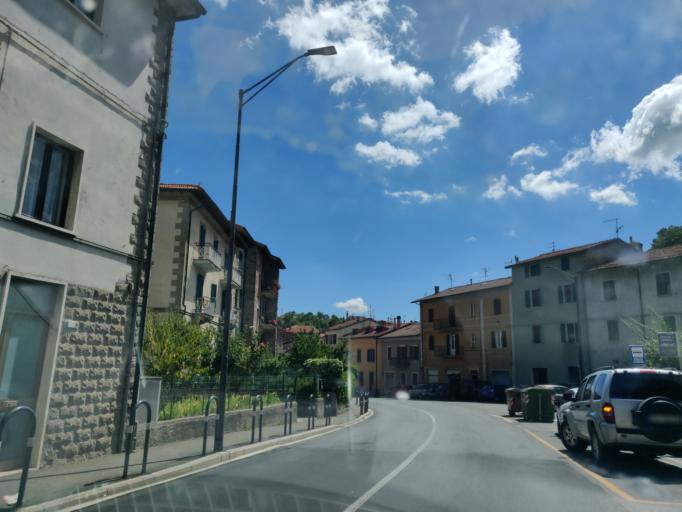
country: IT
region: Tuscany
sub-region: Provincia di Siena
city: Abbadia San Salvatore
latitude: 42.8783
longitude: 11.6773
